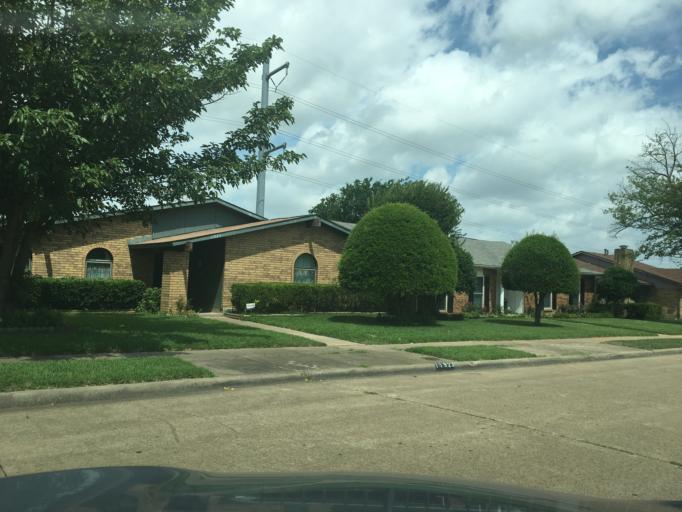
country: US
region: Texas
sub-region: Dallas County
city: Richardson
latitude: 32.9112
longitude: -96.7082
